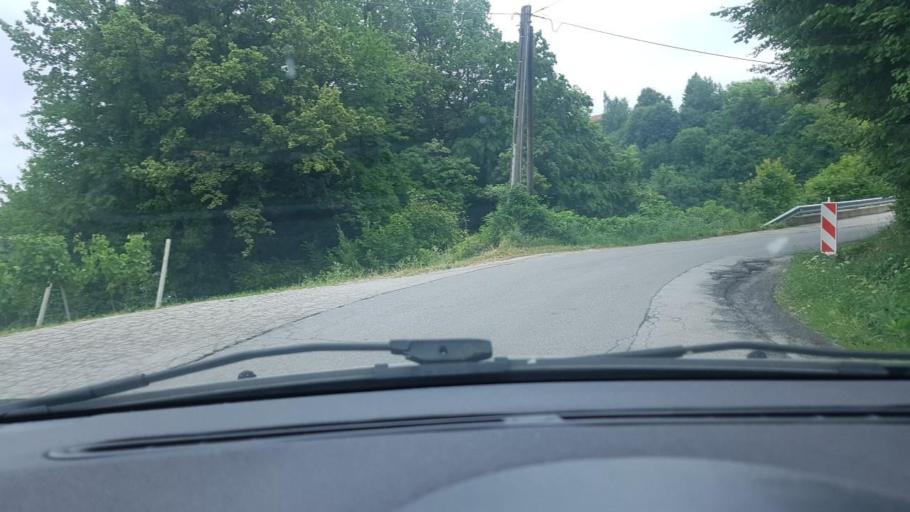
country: SI
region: Podlehnik
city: Podlehnik
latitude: 46.3302
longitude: 15.8959
